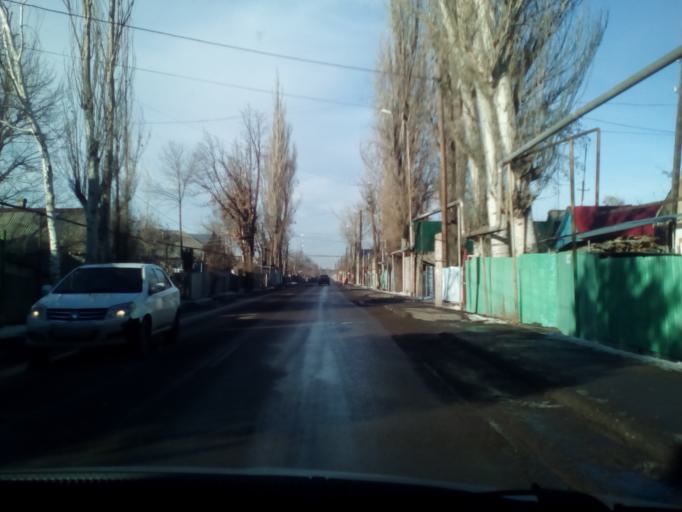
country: KZ
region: Almaty Oblysy
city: Burunday
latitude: 43.1650
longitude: 76.4171
